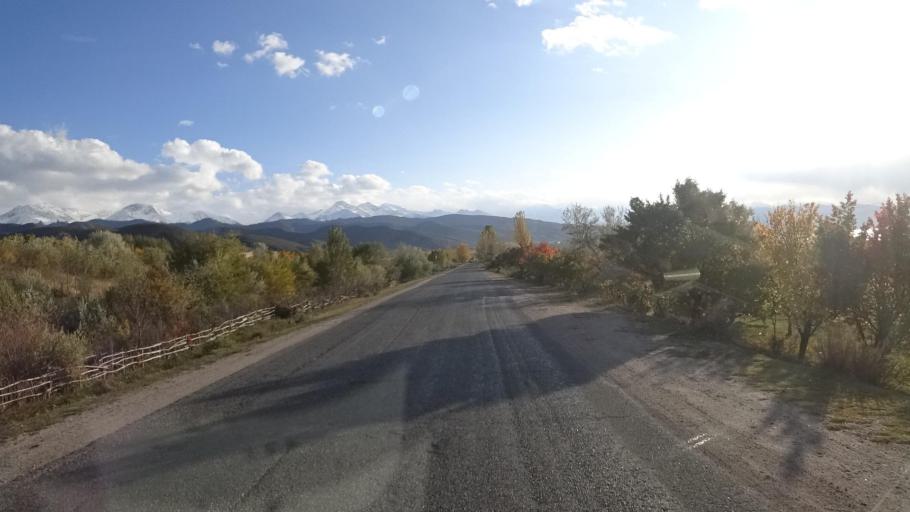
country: KG
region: Ysyk-Koel
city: Pokrovka
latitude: 42.2297
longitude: 77.7151
